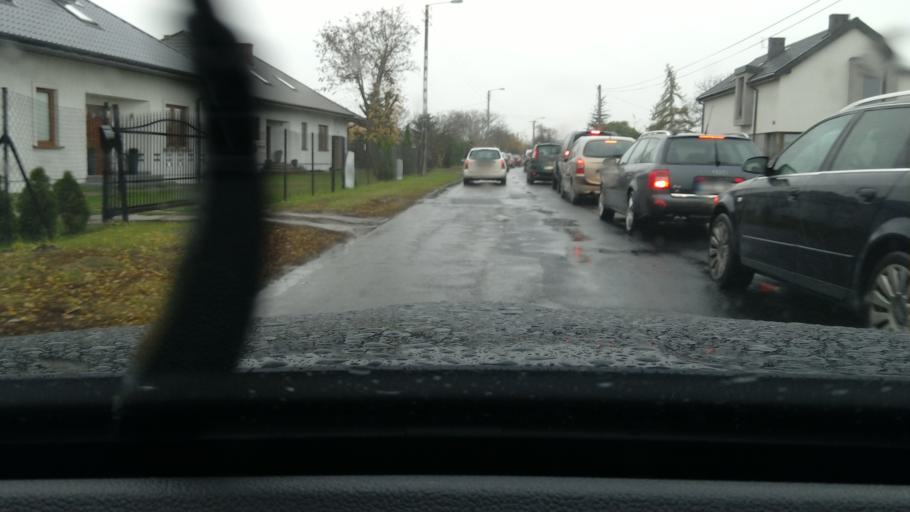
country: PL
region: Lodz Voivodeship
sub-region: Skierniewice
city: Skierniewice
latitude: 51.9435
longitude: 20.1521
